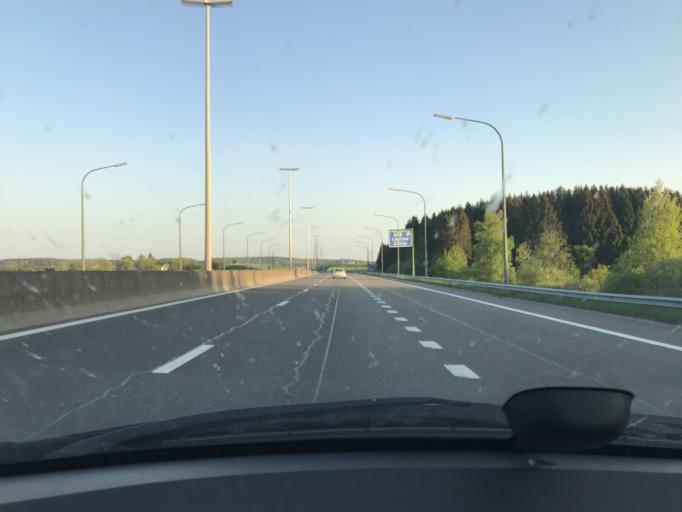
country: BE
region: Wallonia
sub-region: Province du Luxembourg
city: Leglise
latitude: 49.8139
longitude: 5.5157
